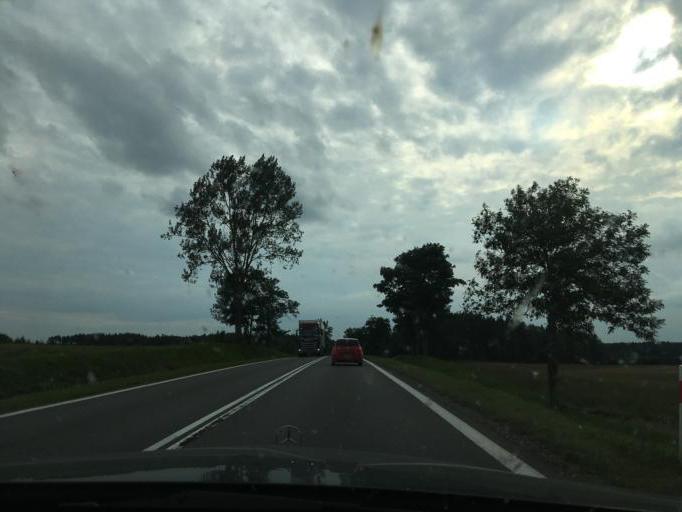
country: PL
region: Podlasie
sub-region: Powiat kolnenski
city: Stawiski
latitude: 53.4520
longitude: 22.1881
